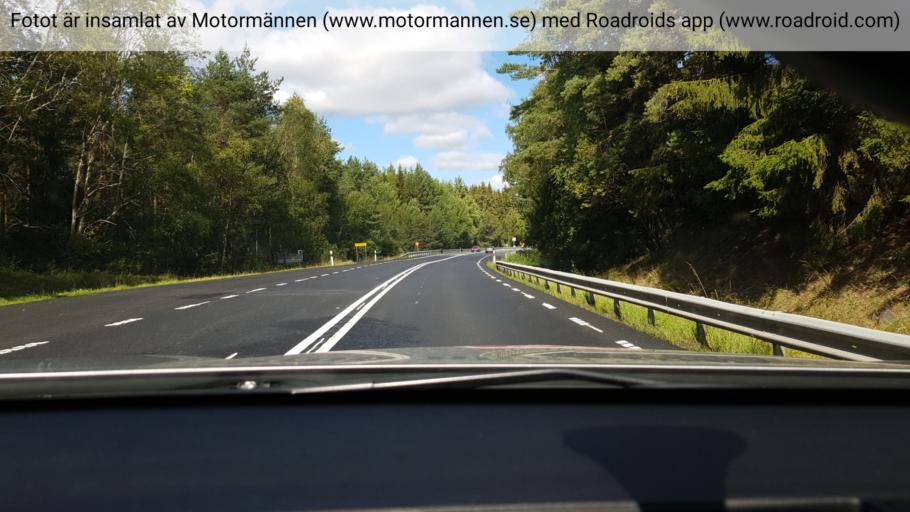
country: SE
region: Stockholm
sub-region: Lidingo
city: Brevik
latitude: 59.4334
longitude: 18.2195
